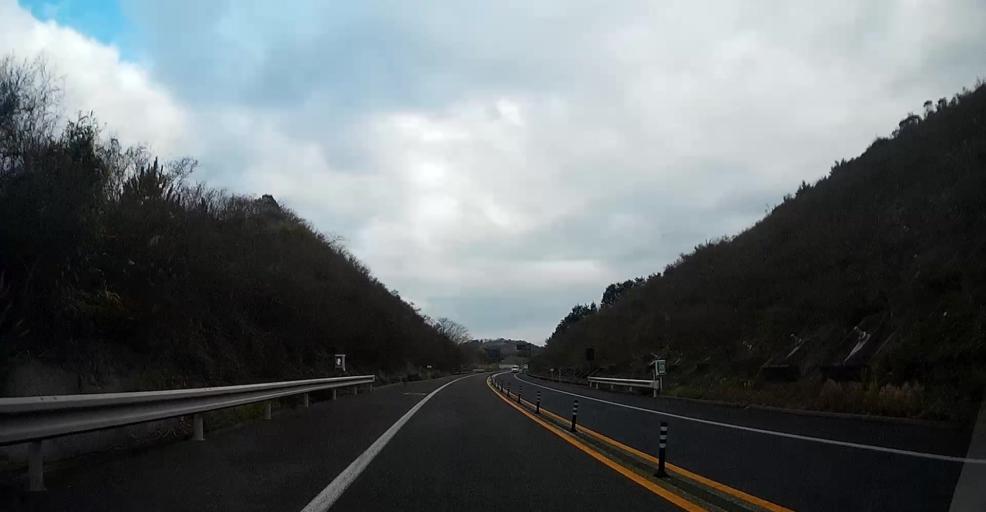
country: JP
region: Kumamoto
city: Hondo
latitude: 32.5099
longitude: 130.3210
